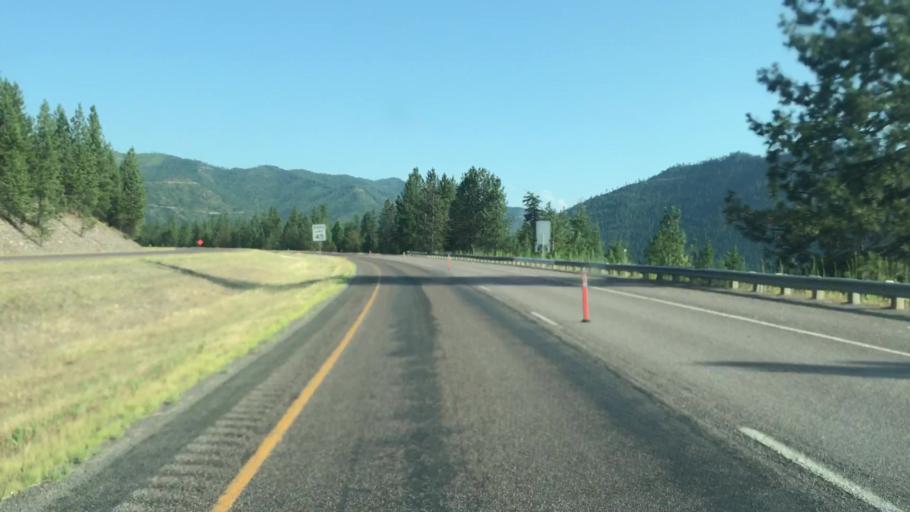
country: US
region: Montana
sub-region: Mineral County
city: Superior
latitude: 47.0178
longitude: -114.7359
